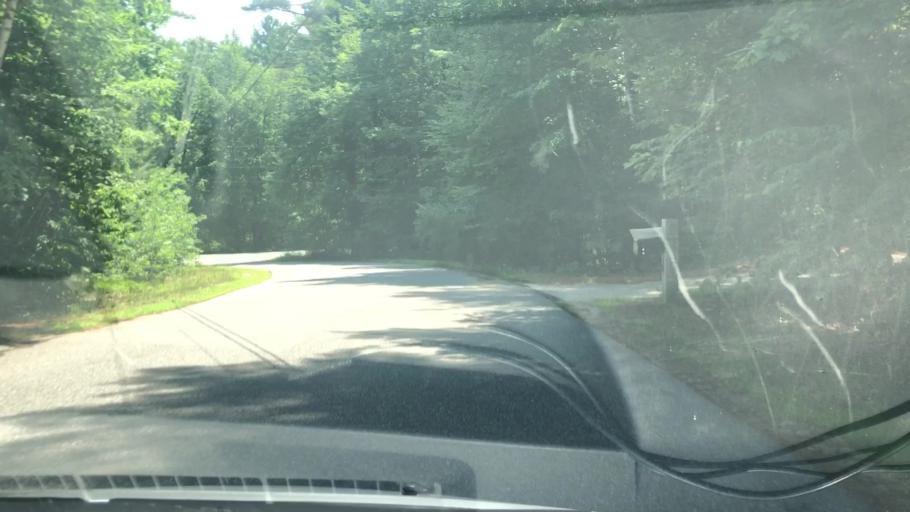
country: US
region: New Hampshire
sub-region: Hillsborough County
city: Milford
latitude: 42.8764
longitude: -71.6151
